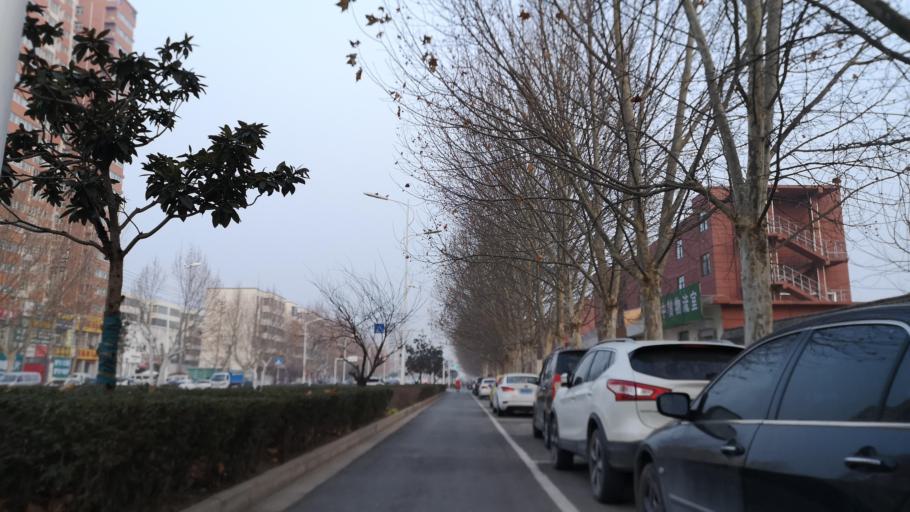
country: CN
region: Henan Sheng
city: Puyang
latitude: 35.7485
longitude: 115.0364
